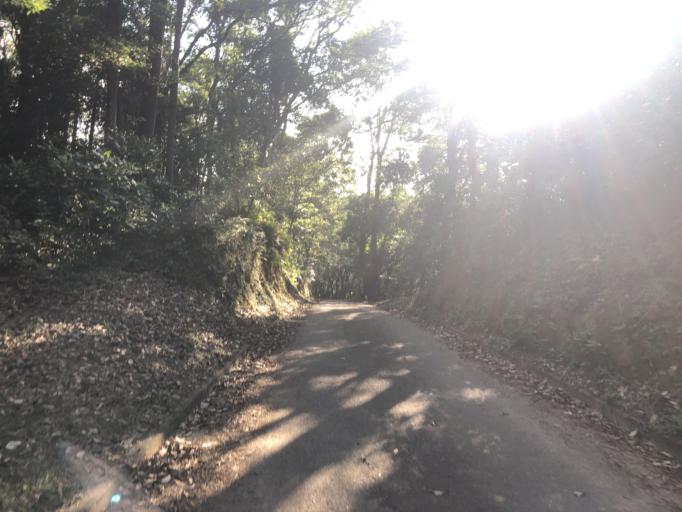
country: HK
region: Tsuen Wan
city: Tsuen Wan
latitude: 22.4004
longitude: 114.0832
